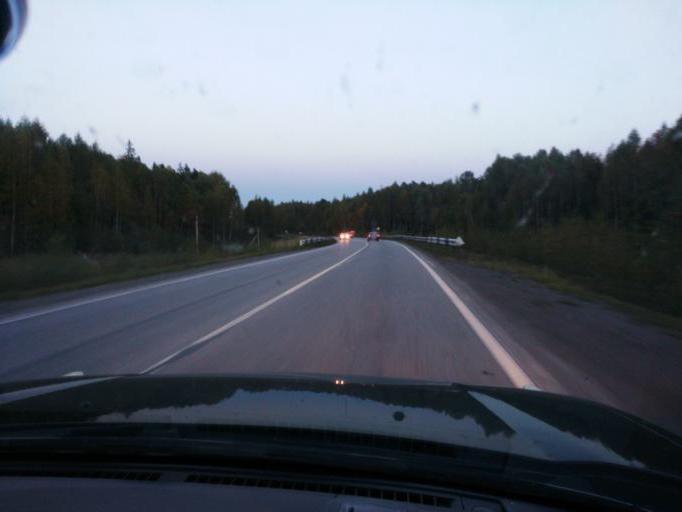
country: RU
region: Perm
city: Verkhnechusovskiye Gorodki
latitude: 58.2456
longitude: 57.0265
